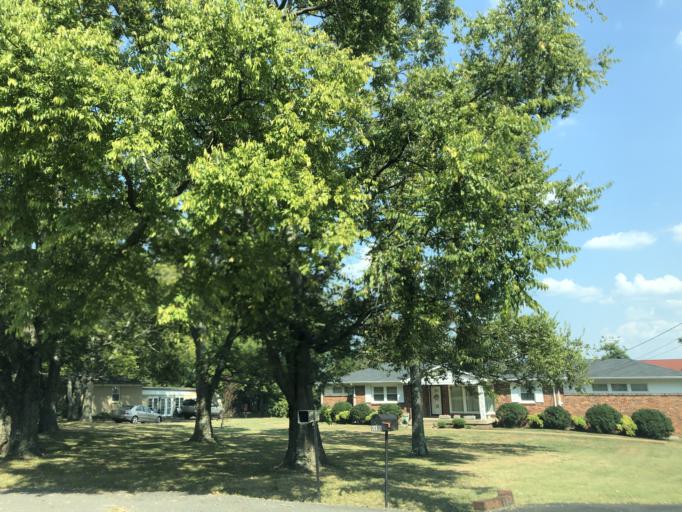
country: US
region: Tennessee
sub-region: Davidson County
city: Oak Hill
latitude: 36.0863
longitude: -86.7646
